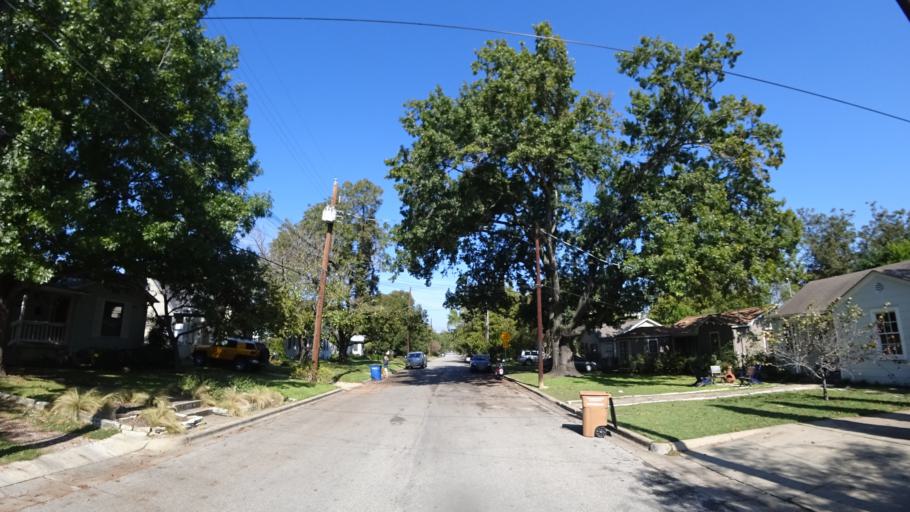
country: US
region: Texas
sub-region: Travis County
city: Austin
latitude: 30.2556
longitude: -97.7684
